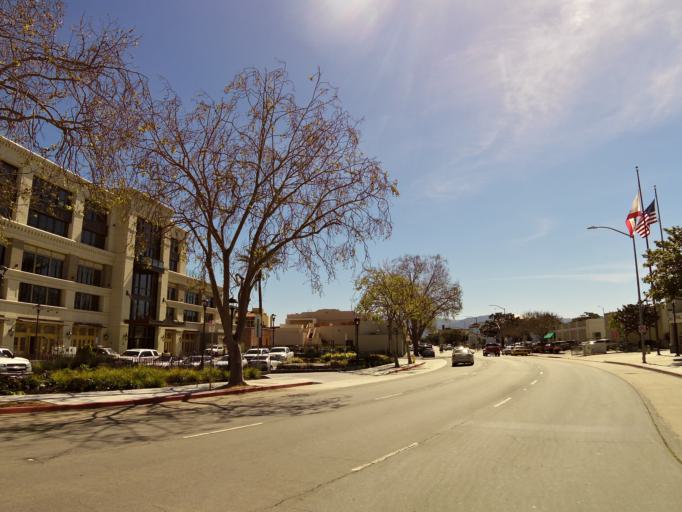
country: US
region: California
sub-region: Monterey County
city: Salinas
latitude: 36.6767
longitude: -121.6566
